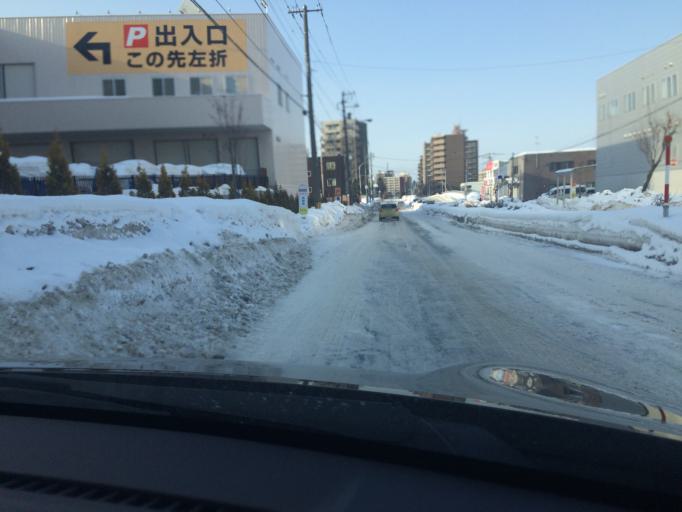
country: JP
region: Hokkaido
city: Ebetsu
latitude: 43.0468
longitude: 141.4755
